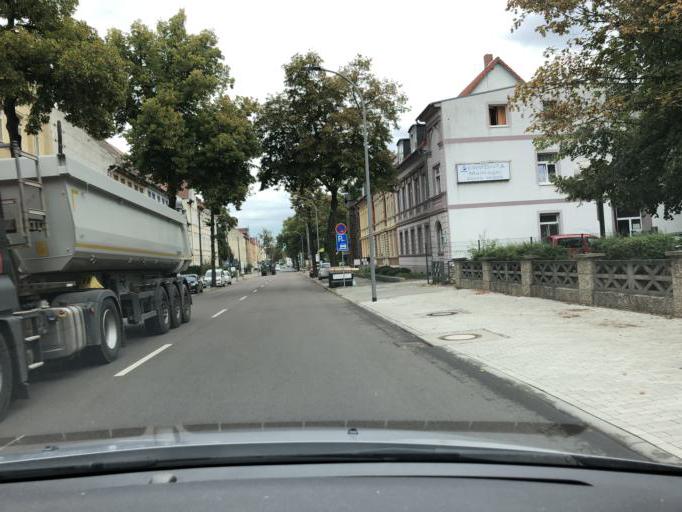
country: DE
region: Saxony-Anhalt
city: Koethen
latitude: 51.7465
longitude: 11.9815
